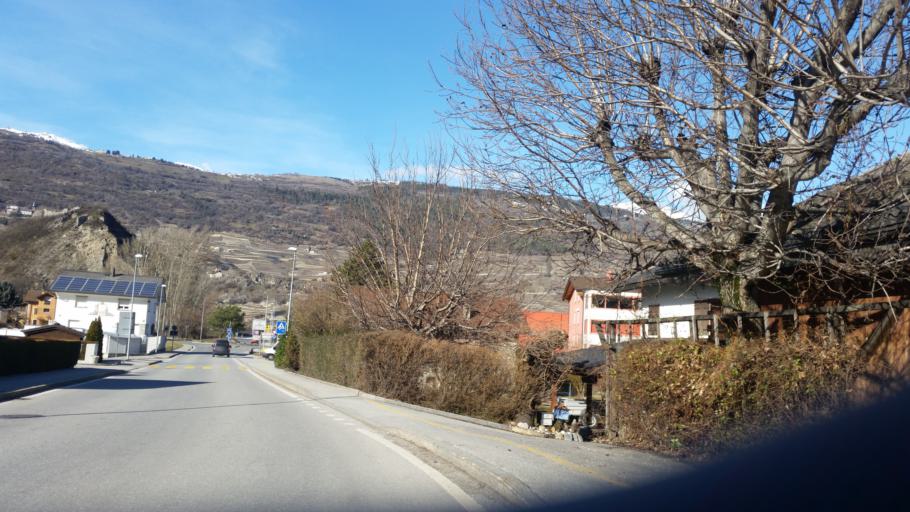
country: CH
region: Valais
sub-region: Sierre District
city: Grone
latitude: 46.2558
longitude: 7.4684
